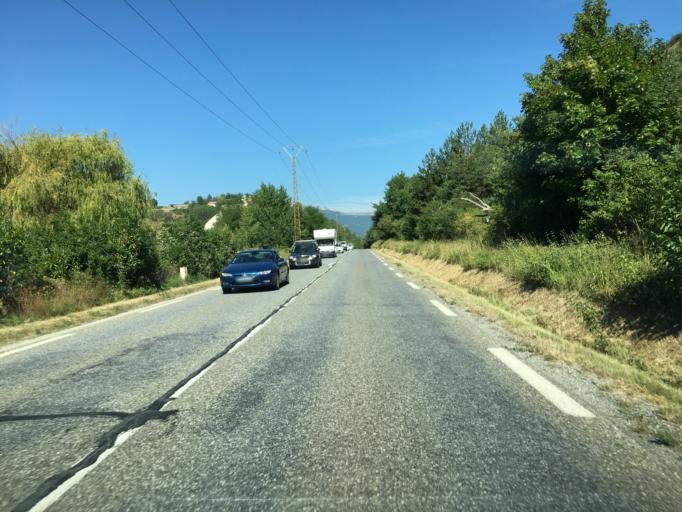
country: FR
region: Provence-Alpes-Cote d'Azur
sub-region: Departement des Hautes-Alpes
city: Laragne-Monteglin
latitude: 44.3358
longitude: 5.7828
